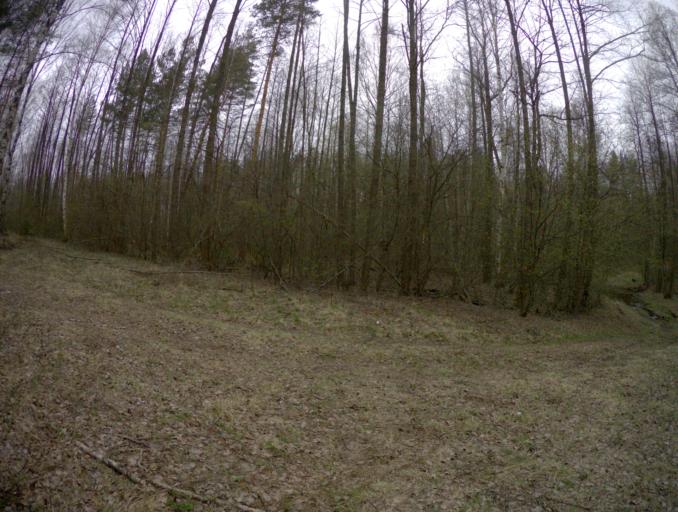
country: RU
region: Vladimir
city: Sudogda
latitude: 56.0376
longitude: 40.7932
